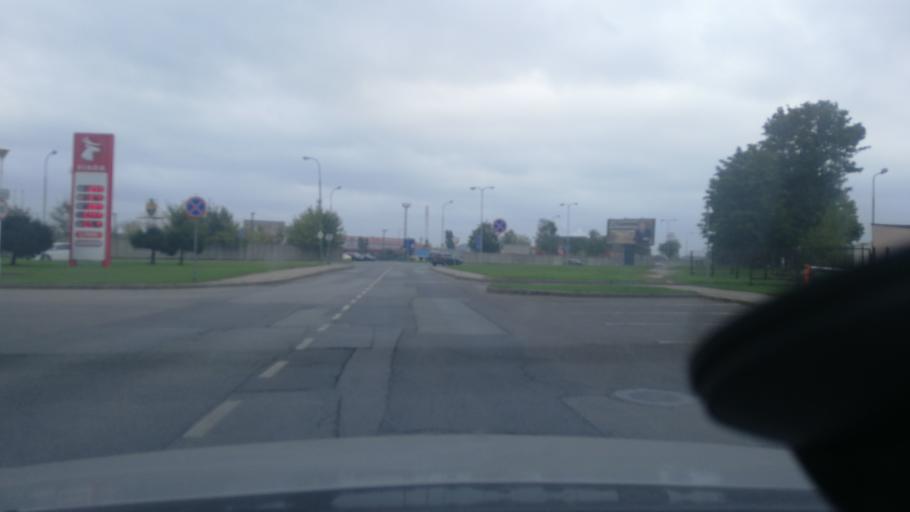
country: LT
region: Klaipedos apskritis
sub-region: Klaipeda
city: Klaipeda
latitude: 55.7190
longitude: 21.1413
